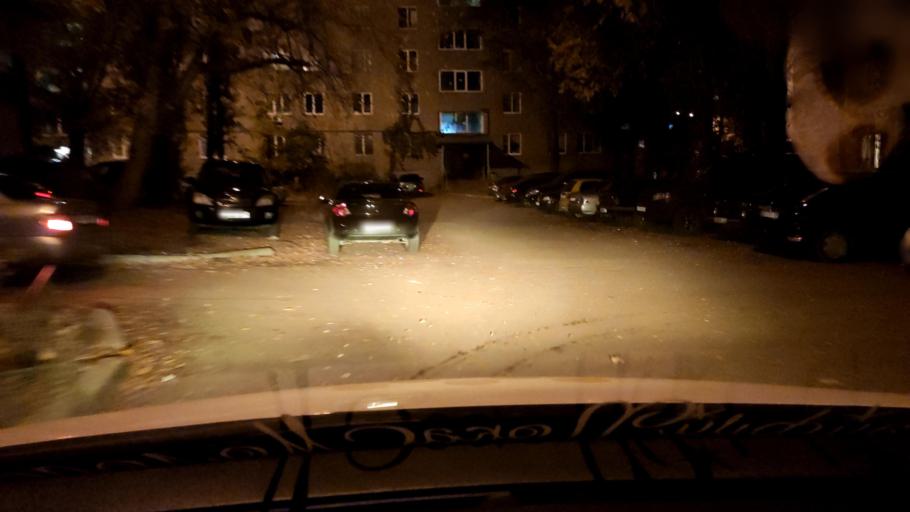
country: RU
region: Voronezj
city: Podgornoye
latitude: 51.7043
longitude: 39.1667
